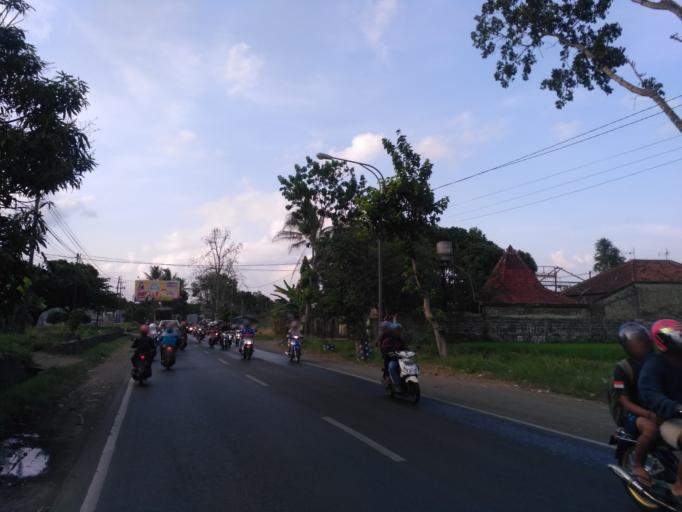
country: ID
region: East Java
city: Wadung
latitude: -8.0419
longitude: 112.6087
